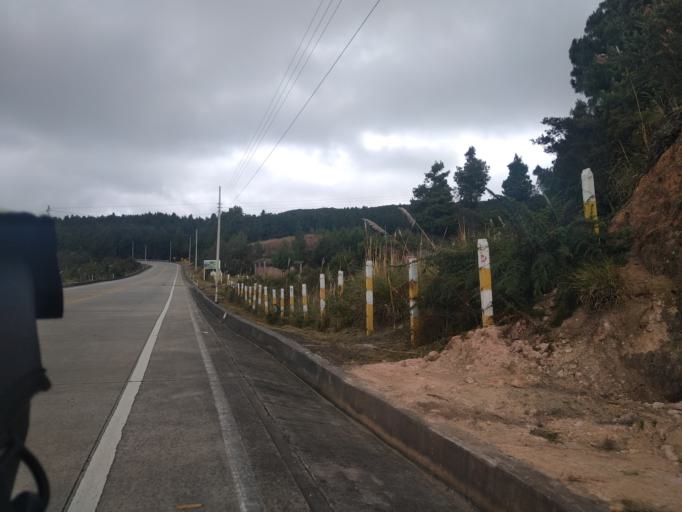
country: EC
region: Azuay
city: Cuenca
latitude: -3.3637
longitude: -79.1944
